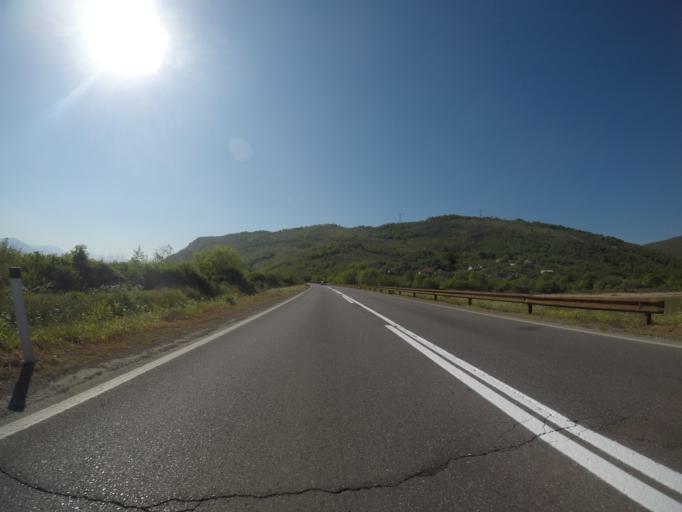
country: ME
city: Spuz
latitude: 42.4624
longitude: 19.1763
